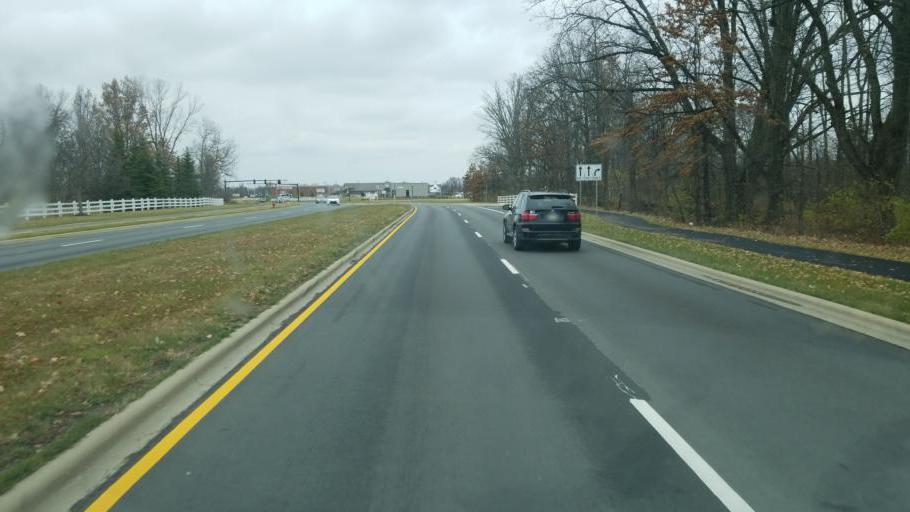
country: US
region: Ohio
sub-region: Delaware County
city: Powell
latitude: 40.1646
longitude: -83.0883
